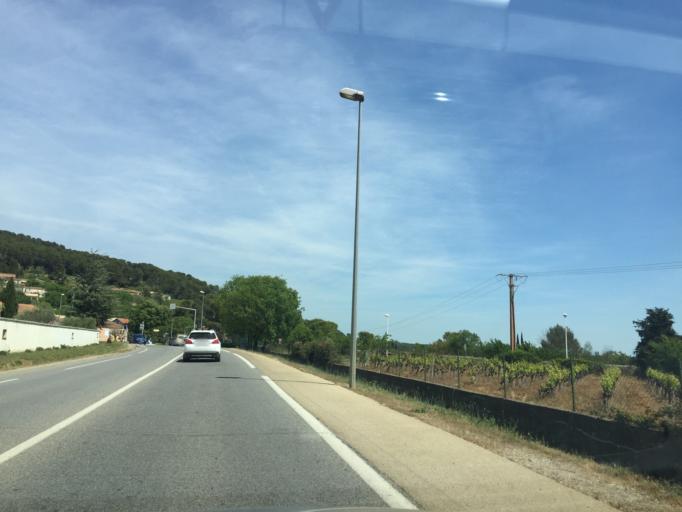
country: FR
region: Provence-Alpes-Cote d'Azur
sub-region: Departement du Var
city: Lorgues
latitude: 43.4913
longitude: 6.3670
